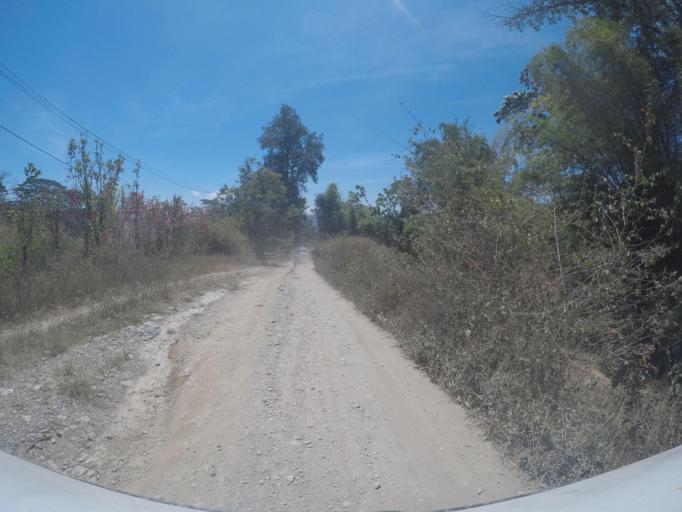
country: TL
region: Ermera
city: Gleno
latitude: -8.7331
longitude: 125.4129
